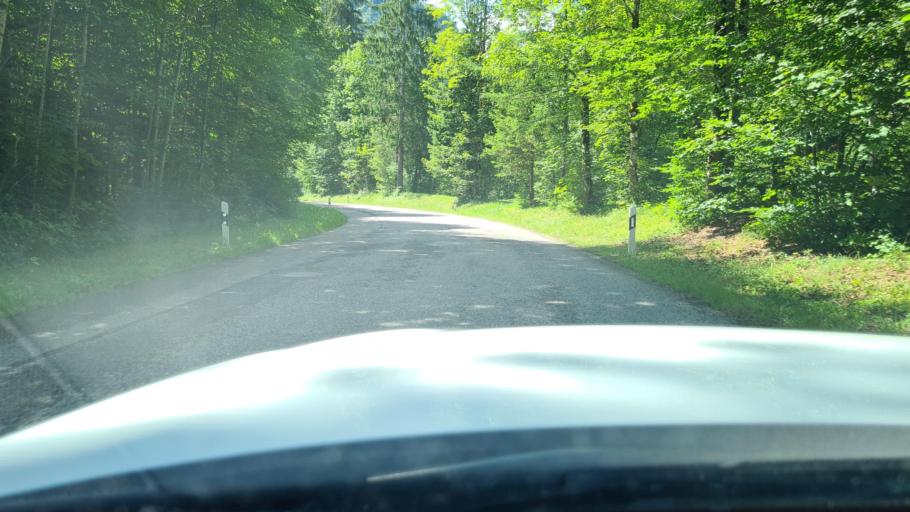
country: DE
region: Bavaria
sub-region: Swabia
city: Oberstdorf
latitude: 47.3812
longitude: 10.2807
